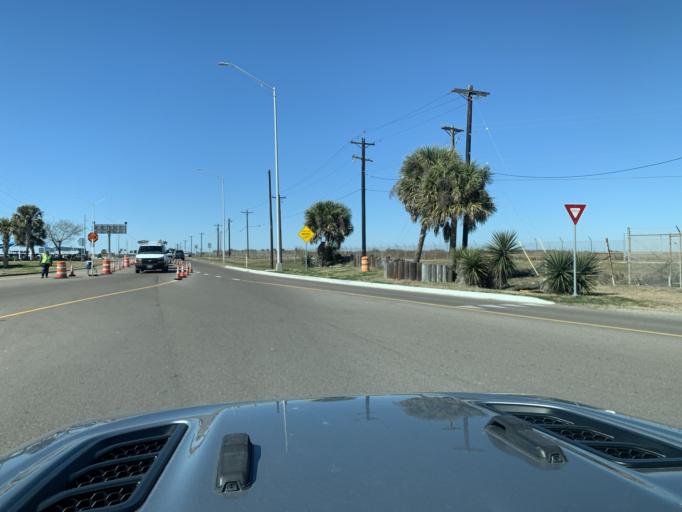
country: US
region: Texas
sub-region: Nueces County
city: Port Aransas
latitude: 27.8449
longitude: -97.0711
